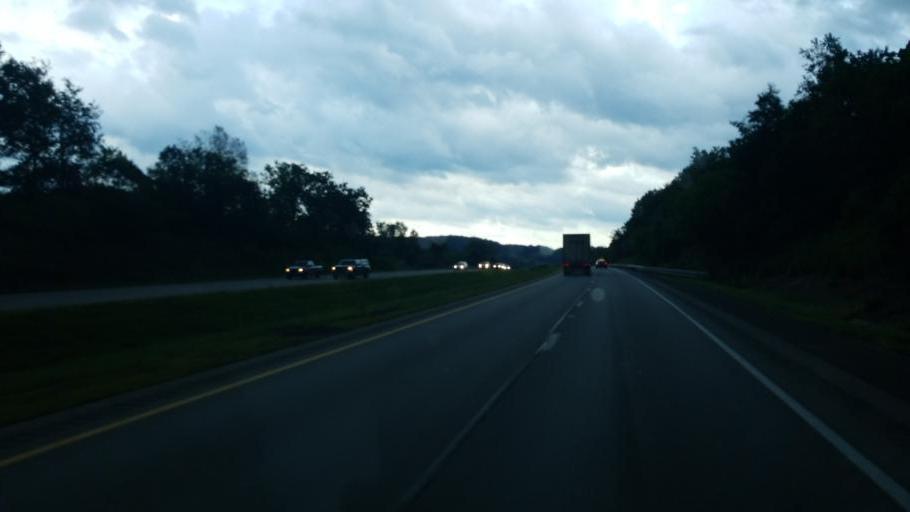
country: US
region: Pennsylvania
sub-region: Butler County
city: Zelienople
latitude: 40.8585
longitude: -80.1083
